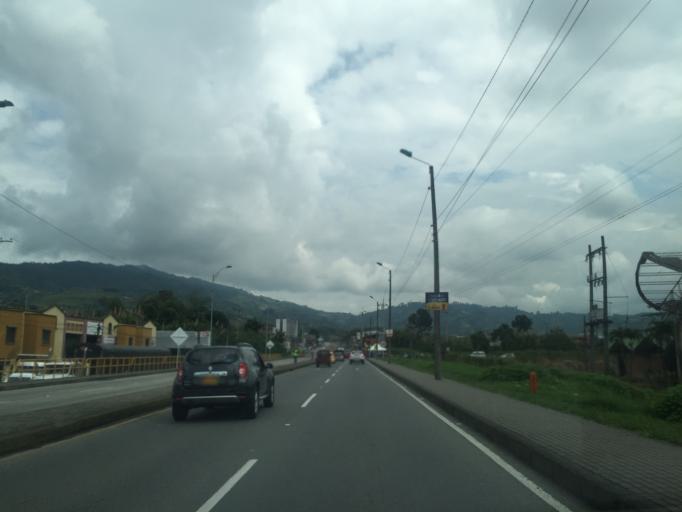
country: CO
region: Risaralda
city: Dos Quebradas
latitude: 4.8384
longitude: -75.6756
